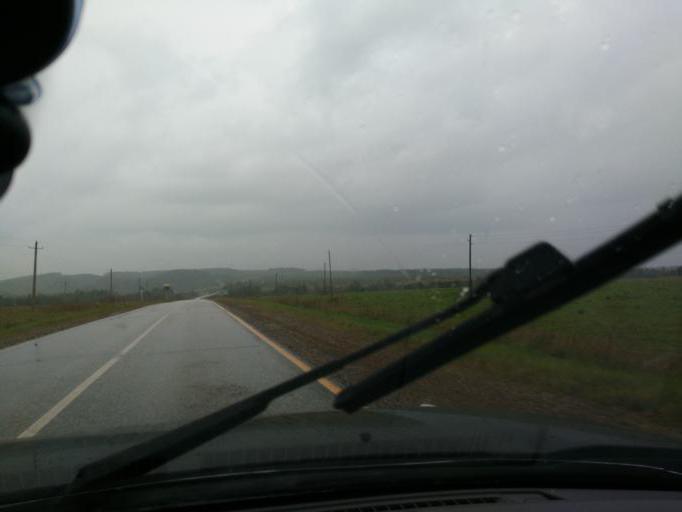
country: RU
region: Perm
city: Barda
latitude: 57.1022
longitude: 55.5281
